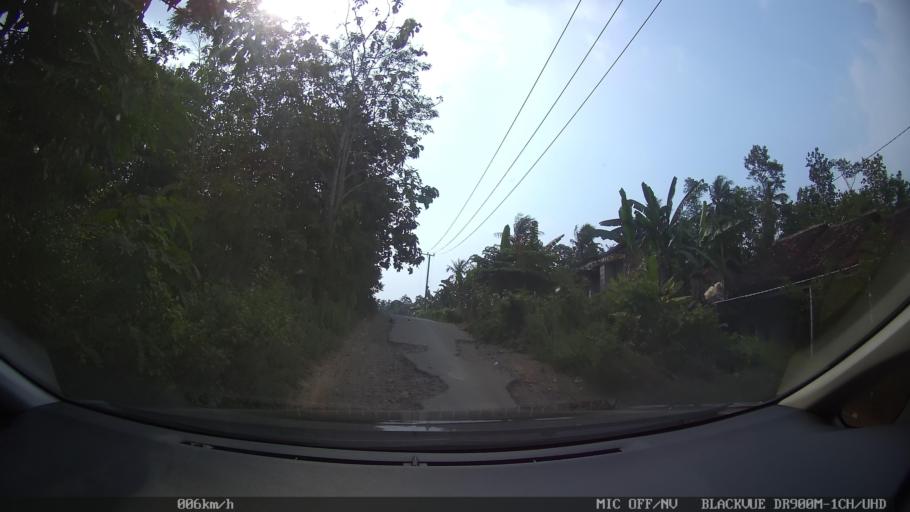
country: ID
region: Lampung
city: Gadingrejo
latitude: -5.3968
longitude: 105.0240
